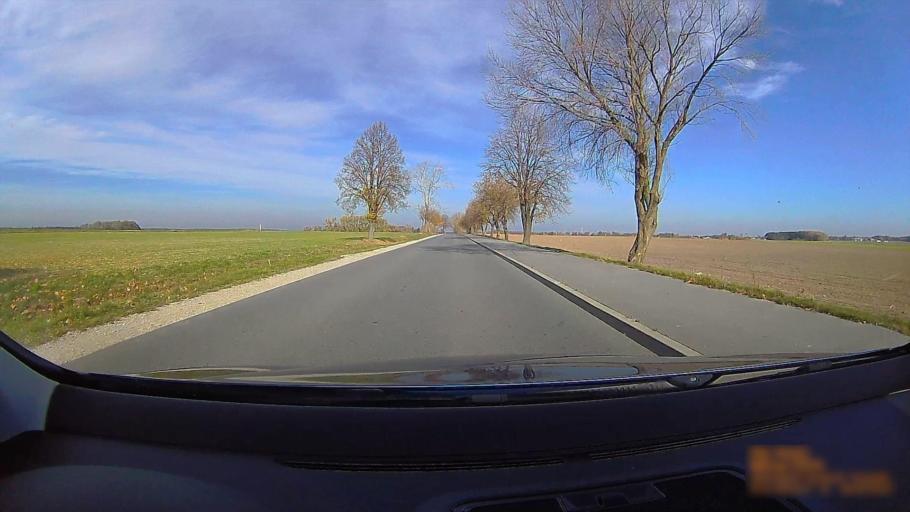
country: PL
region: Greater Poland Voivodeship
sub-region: Powiat kepinski
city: Kepno
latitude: 51.3370
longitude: 18.0206
